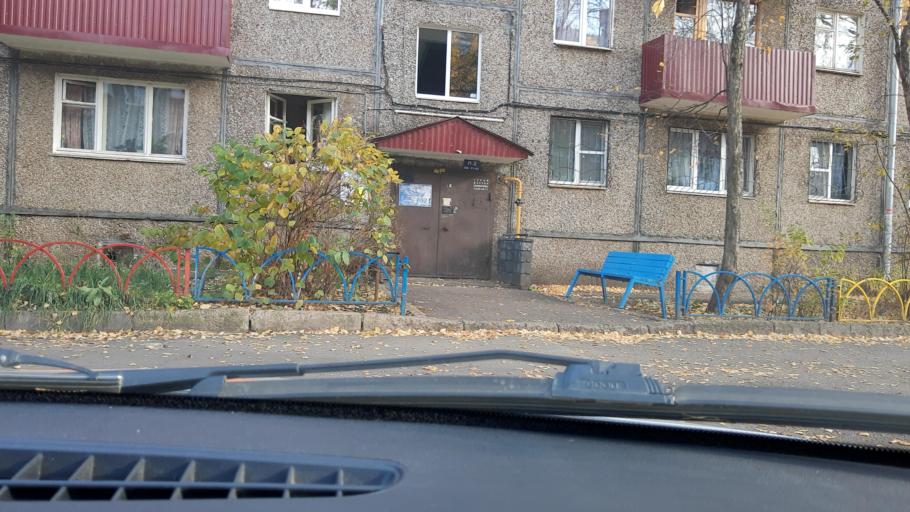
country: RU
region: Bashkortostan
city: Ufa
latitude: 54.7441
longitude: 56.0223
